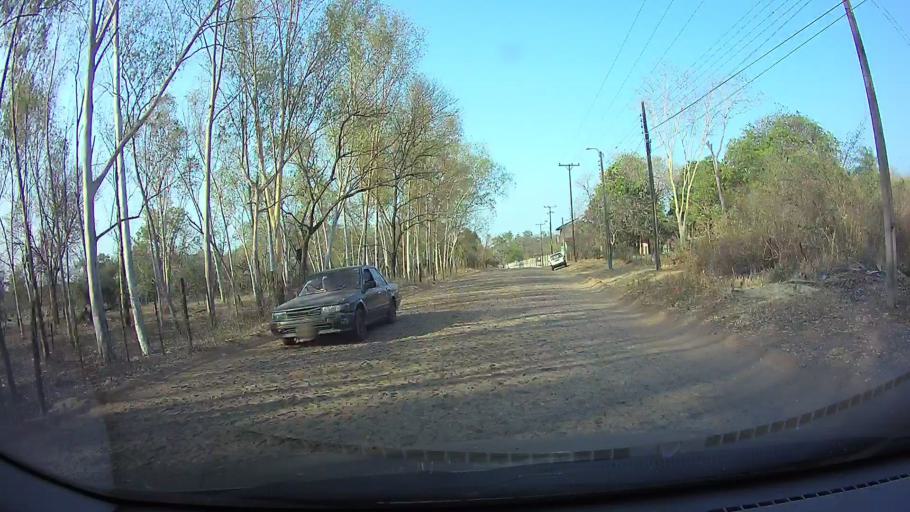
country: PY
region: Central
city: Limpio
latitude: -25.2225
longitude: -57.5056
